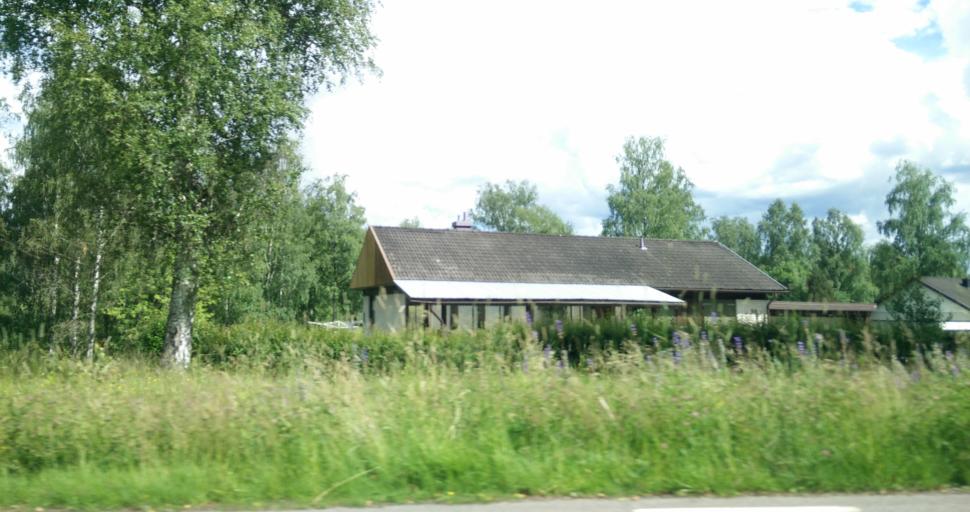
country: SE
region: Vaermland
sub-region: Hagfors Kommun
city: Hagfors
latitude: 60.0270
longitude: 13.6240
